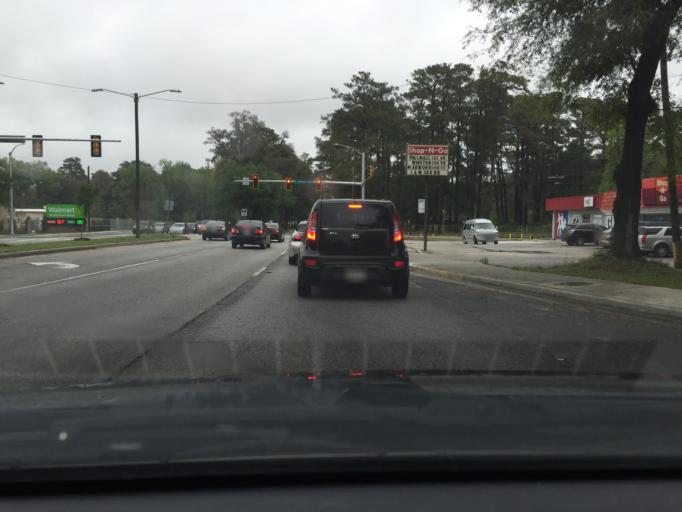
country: US
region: Georgia
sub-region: Chatham County
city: Montgomery
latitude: 31.9823
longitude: -81.1303
